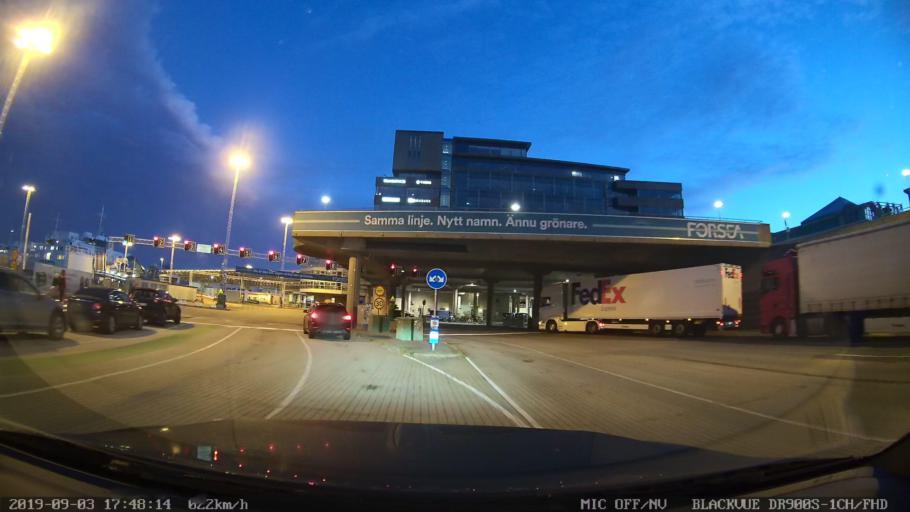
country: SE
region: Skane
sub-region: Helsingborg
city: Helsingborg
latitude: 56.0429
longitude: 12.6939
